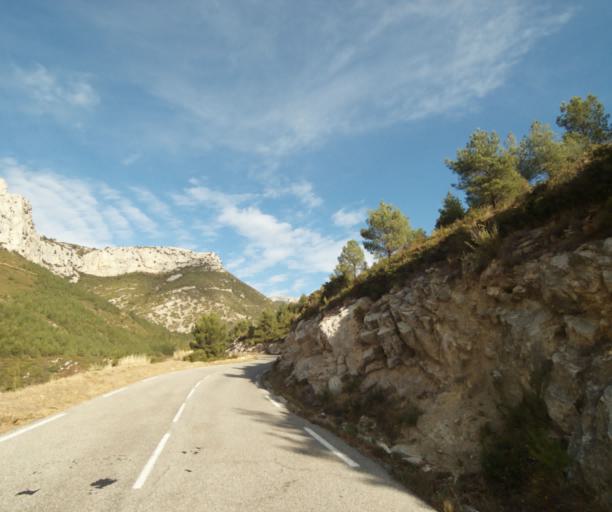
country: FR
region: Provence-Alpes-Cote d'Azur
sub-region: Departement des Bouches-du-Rhone
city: Gemenos
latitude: 43.2954
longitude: 5.6594
